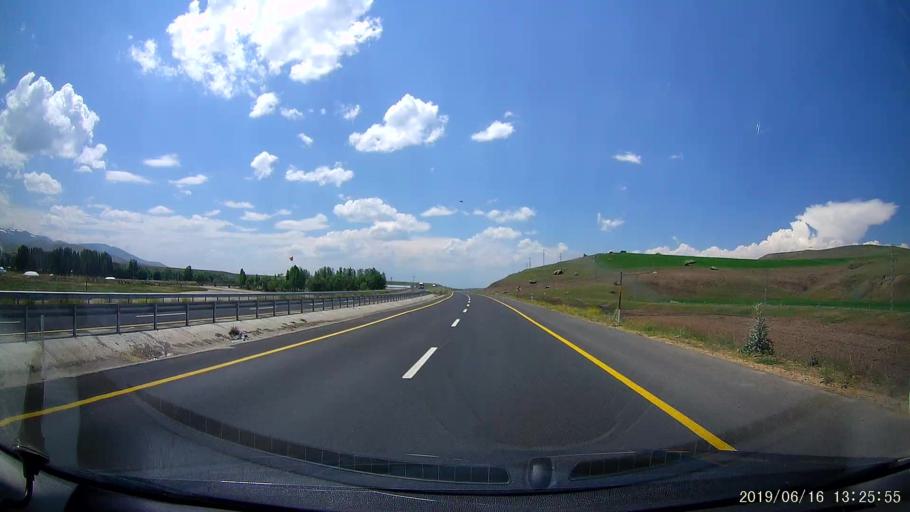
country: TR
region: Agri
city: Taslicay
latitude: 39.6564
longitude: 43.3411
